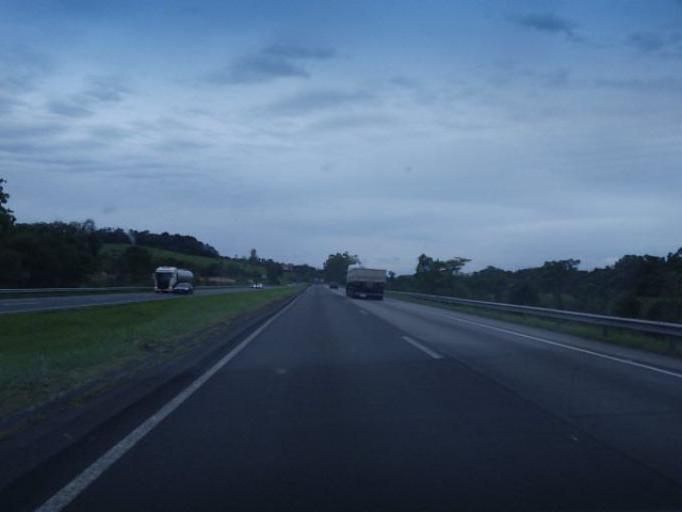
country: BR
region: Sao Paulo
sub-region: Registro
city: Registro
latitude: -24.4145
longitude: -47.7588
